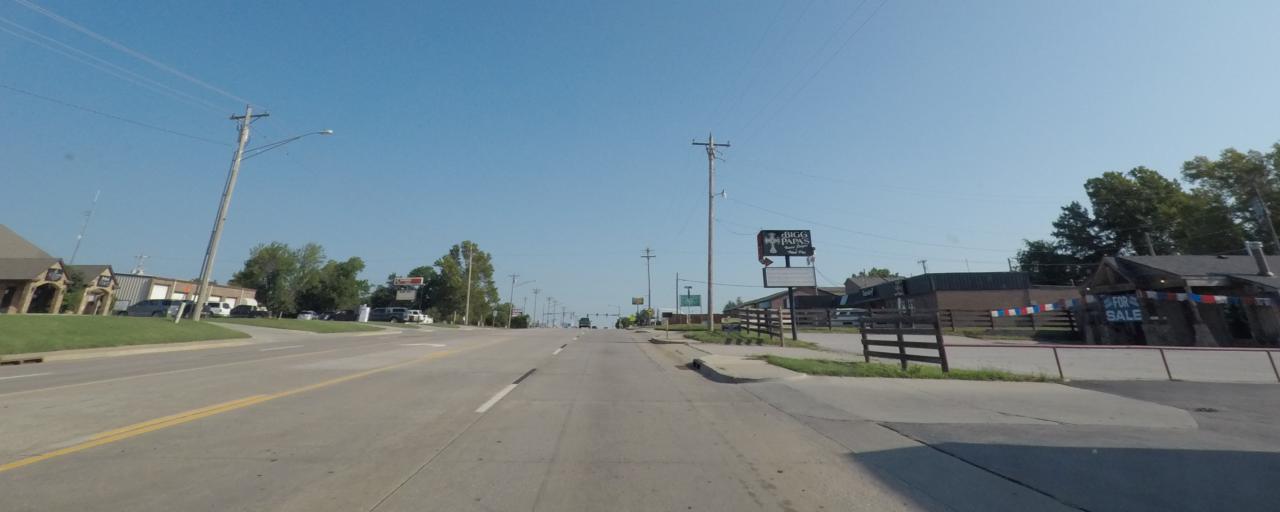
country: US
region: Oklahoma
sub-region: McClain County
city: Newcastle
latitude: 35.2537
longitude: -97.6001
